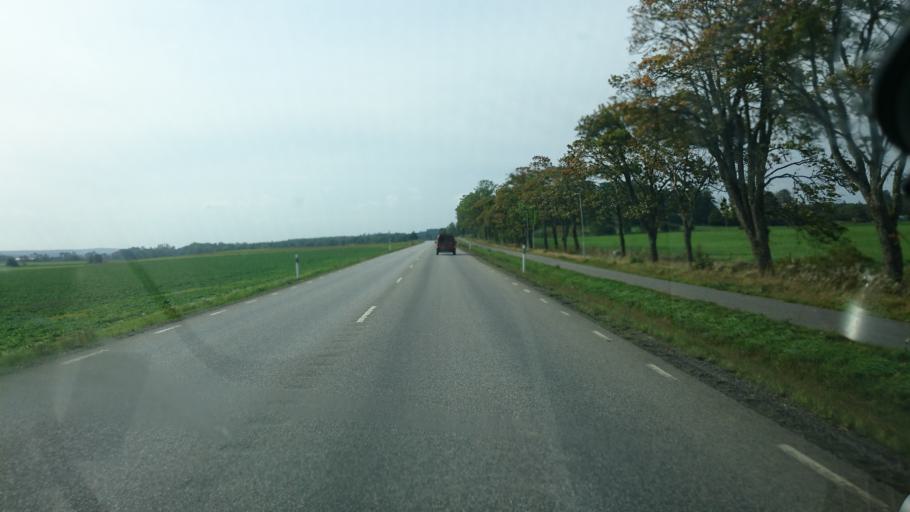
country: SE
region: Vaestra Goetaland
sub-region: Alingsas Kommun
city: Sollebrunn
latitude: 58.0952
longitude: 12.5031
